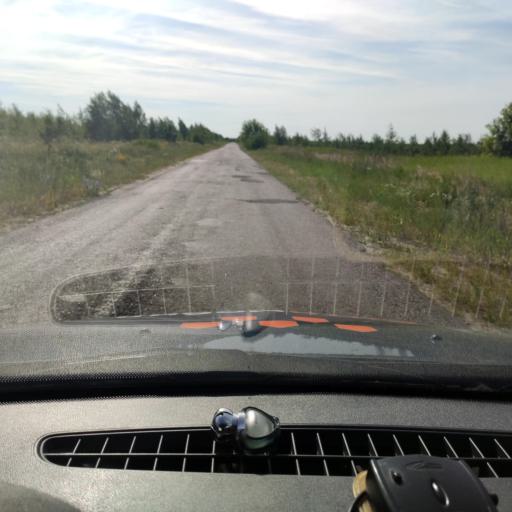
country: RU
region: Voronezj
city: Somovo
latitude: 51.7813
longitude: 39.3941
